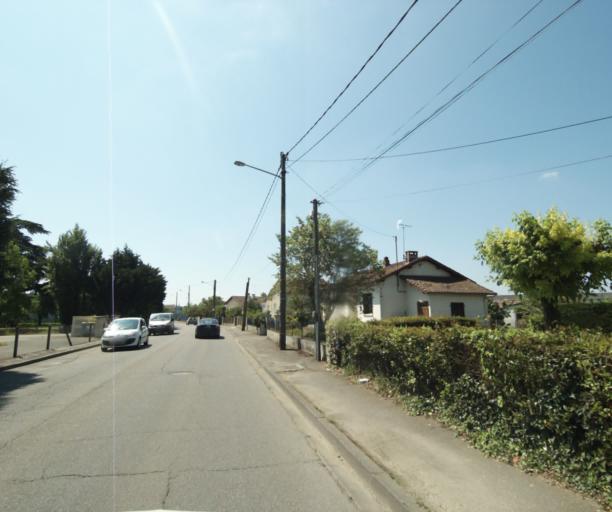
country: FR
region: Midi-Pyrenees
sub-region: Departement du Tarn-et-Garonne
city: Montauban
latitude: 44.0354
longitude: 1.3524
